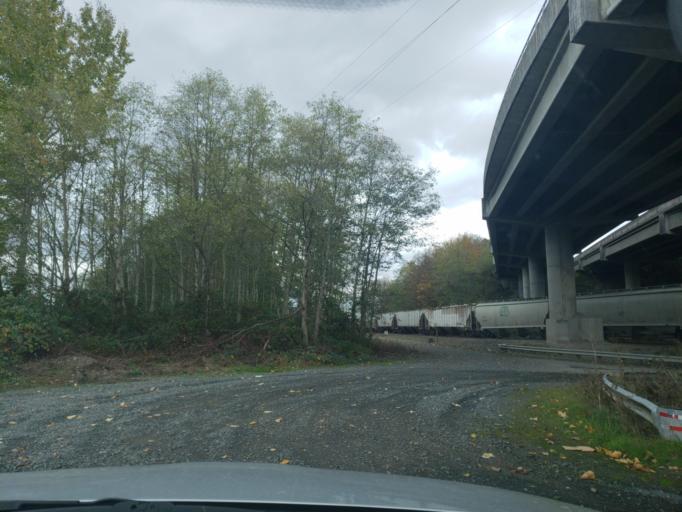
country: US
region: Washington
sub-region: Snohomish County
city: Everett
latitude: 48.0173
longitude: -122.2062
